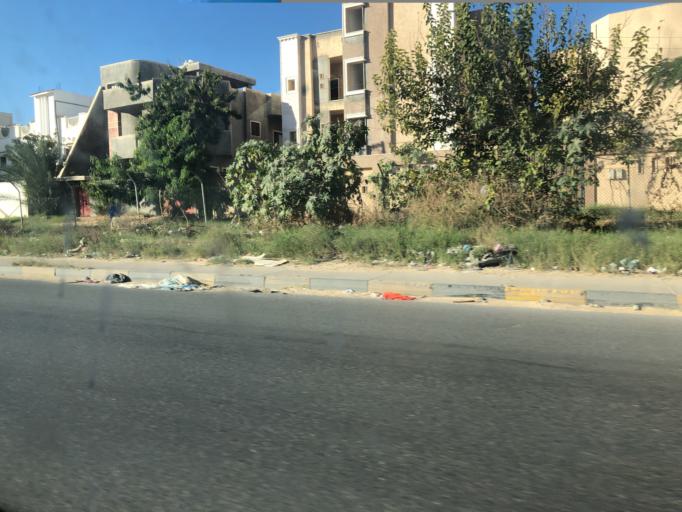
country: LY
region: Tripoli
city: Tripoli
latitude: 32.8688
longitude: 13.2389
